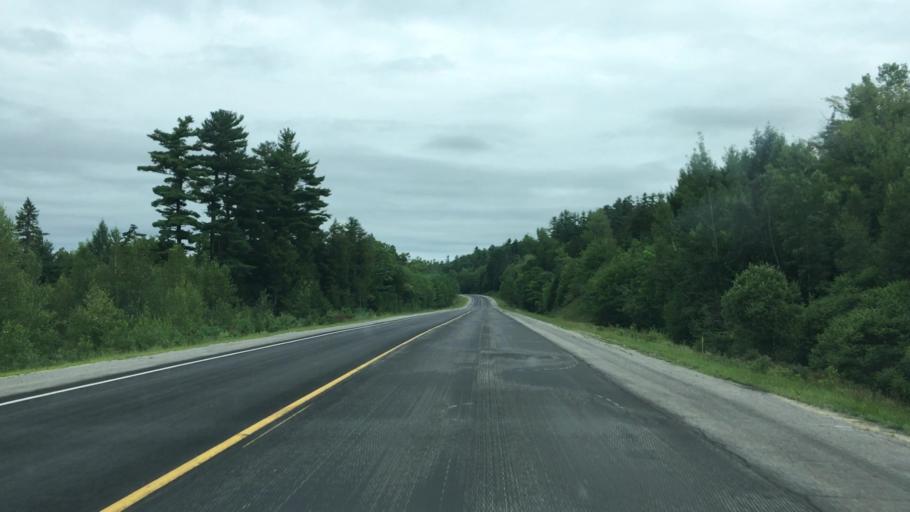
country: US
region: Maine
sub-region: Washington County
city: Cherryfield
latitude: 44.8940
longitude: -67.8560
